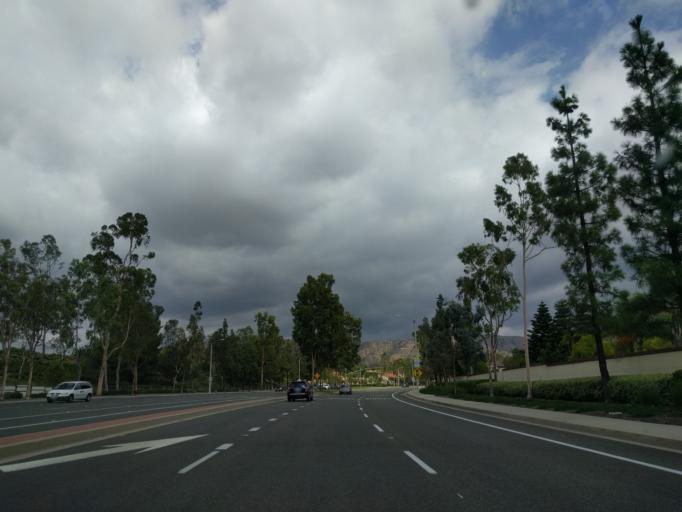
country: US
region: California
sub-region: Orange County
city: North Tustin
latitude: 33.7475
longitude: -117.7734
